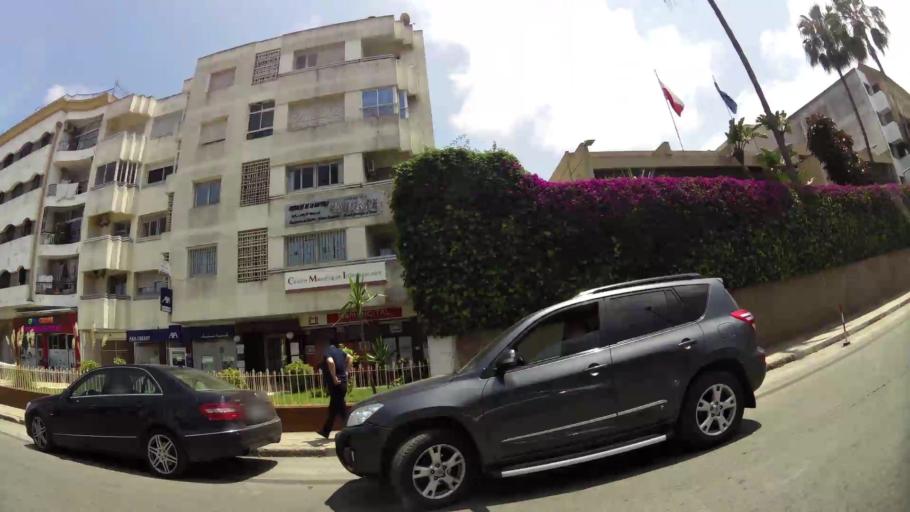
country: MA
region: Rabat-Sale-Zemmour-Zaer
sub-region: Rabat
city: Rabat
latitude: 34.0096
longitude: -6.8441
